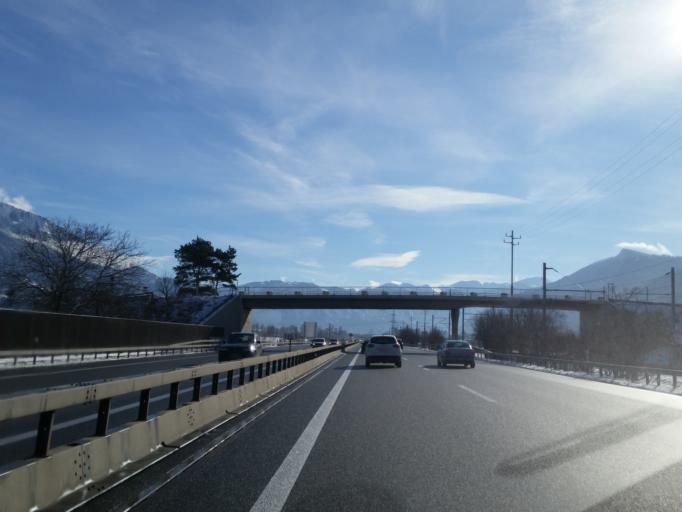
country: CH
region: Saint Gallen
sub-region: Wahlkreis Sarganserland
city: Sargans
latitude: 47.0296
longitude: 9.4718
